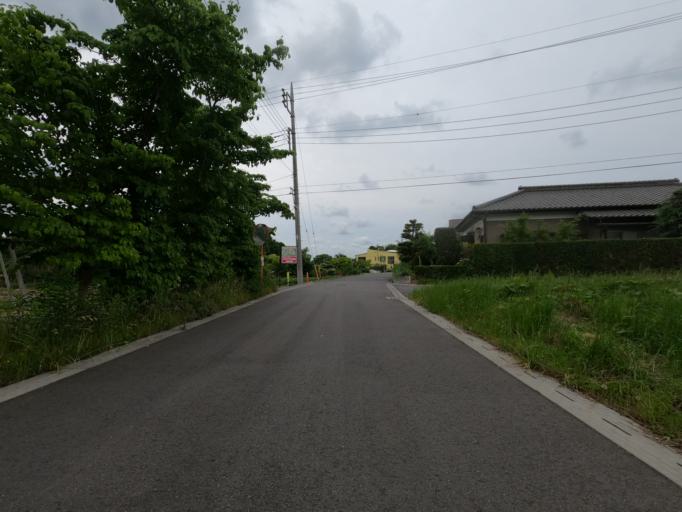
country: JP
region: Ibaraki
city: Moriya
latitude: 35.9494
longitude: 139.9711
